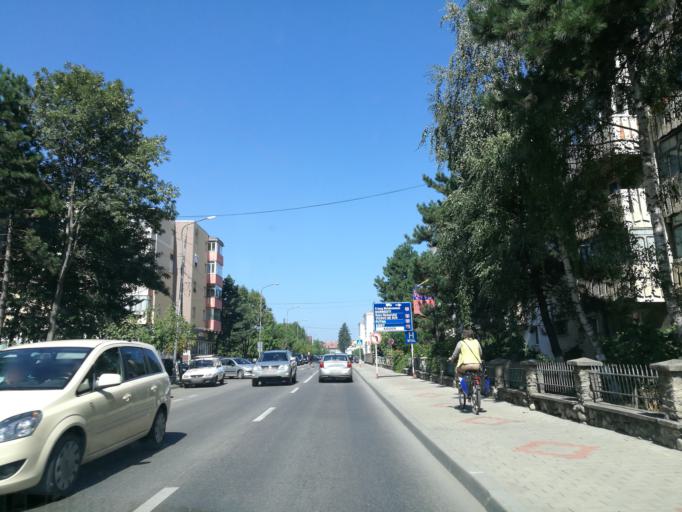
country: RO
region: Suceava
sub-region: Municipiul Suceava
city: Radauti
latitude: 47.8370
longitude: 25.9282
